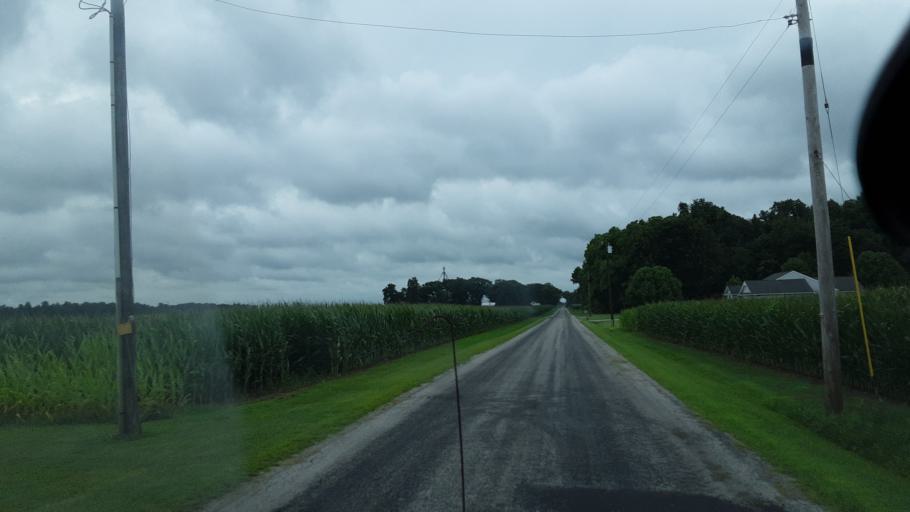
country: US
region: Indiana
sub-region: Wells County
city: Ossian
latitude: 40.8153
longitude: -85.0718
